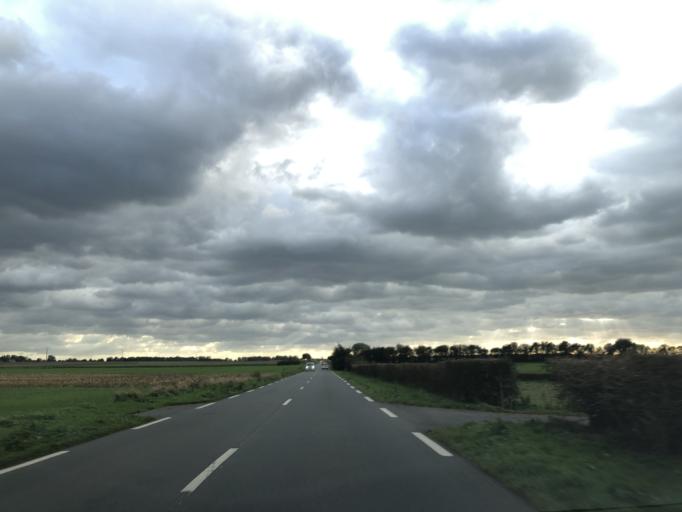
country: FR
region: Picardie
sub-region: Departement de la Somme
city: Ault
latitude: 50.0920
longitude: 1.4587
